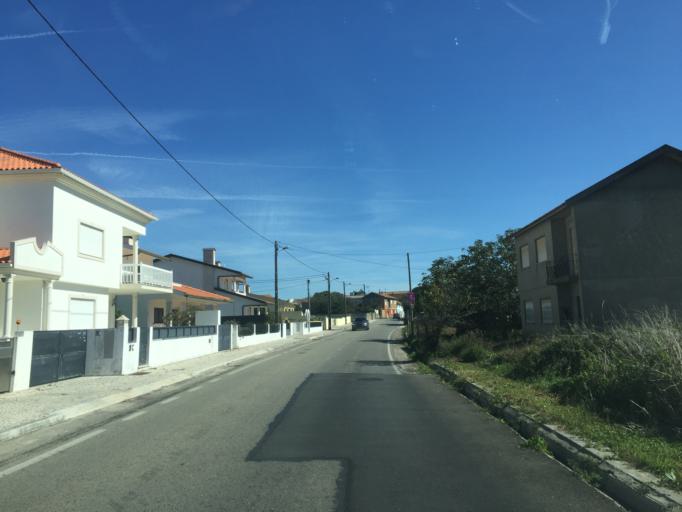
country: PT
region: Coimbra
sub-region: Figueira da Foz
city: Tavarede
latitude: 40.2154
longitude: -8.8589
